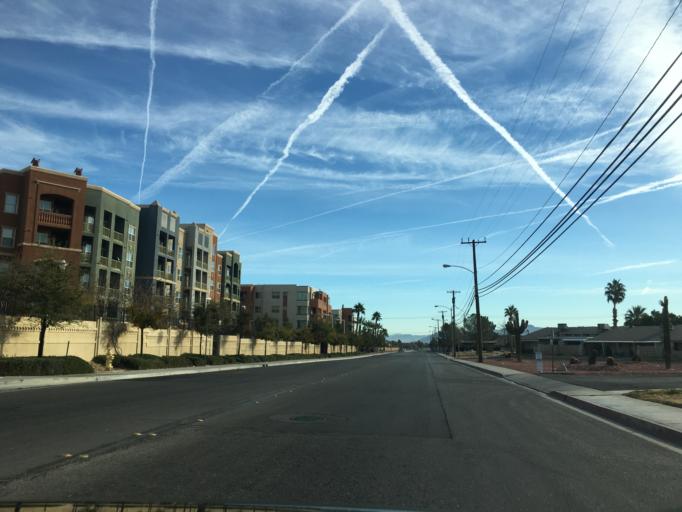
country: US
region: Nevada
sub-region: Clark County
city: Enterprise
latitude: 36.0209
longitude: -115.1705
